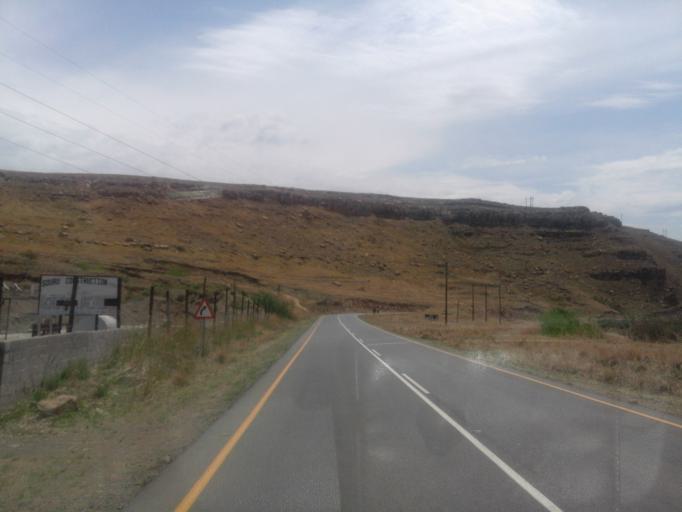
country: LS
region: Qacha's Nek
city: Qacha's Nek
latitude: -30.1056
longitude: 28.6587
